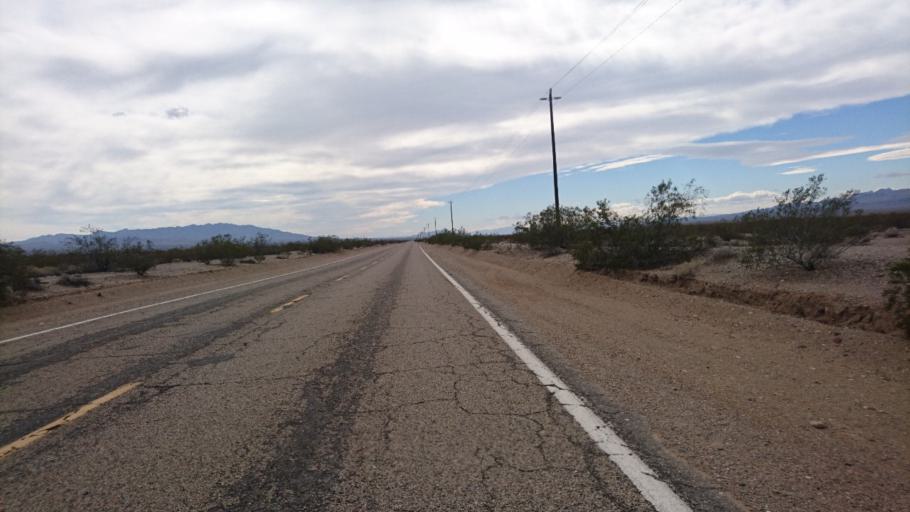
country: US
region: California
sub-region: San Bernardino County
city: Needles
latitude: 34.7947
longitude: -115.1990
